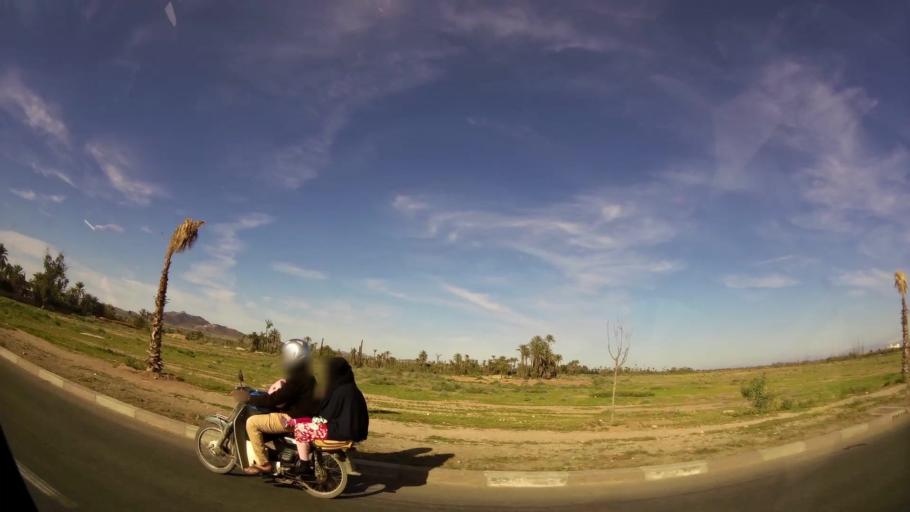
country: MA
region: Marrakech-Tensift-Al Haouz
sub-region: Marrakech
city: Marrakesh
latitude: 31.6919
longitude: -8.0557
